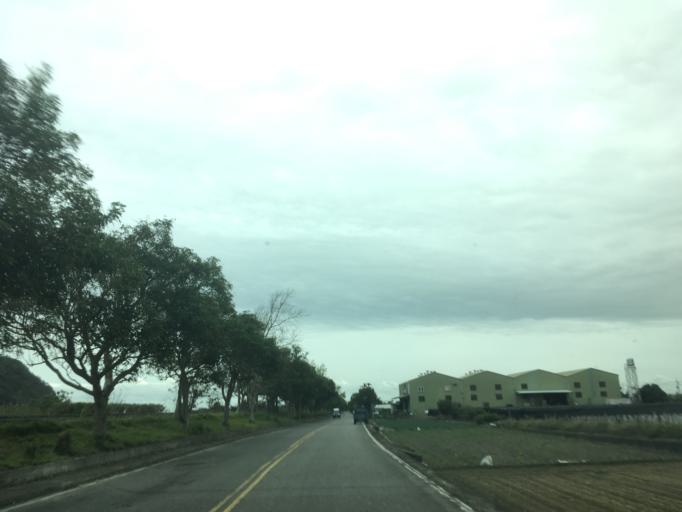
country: TW
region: Taiwan
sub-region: Taitung
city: Taitung
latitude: 22.8031
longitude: 121.1346
